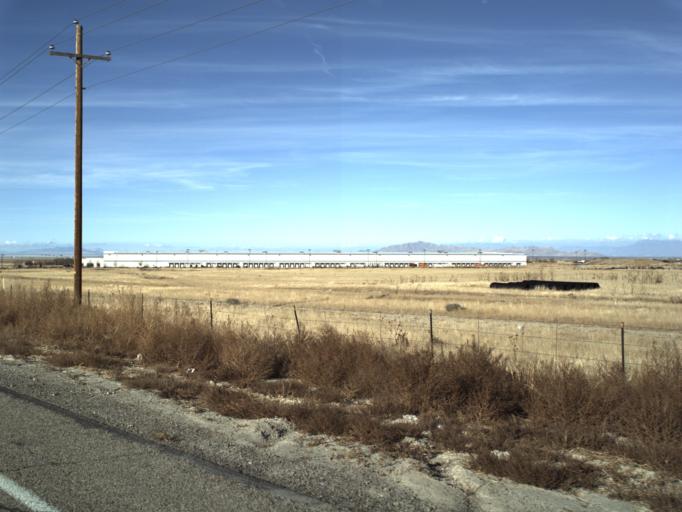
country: US
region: Utah
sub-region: Tooele County
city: Erda
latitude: 40.5801
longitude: -112.3686
